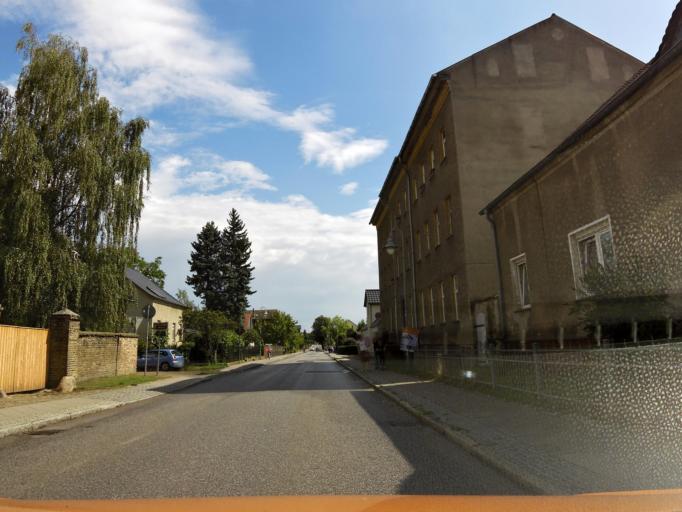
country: DE
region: Brandenburg
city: Ketzin
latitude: 52.4748
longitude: 12.8461
